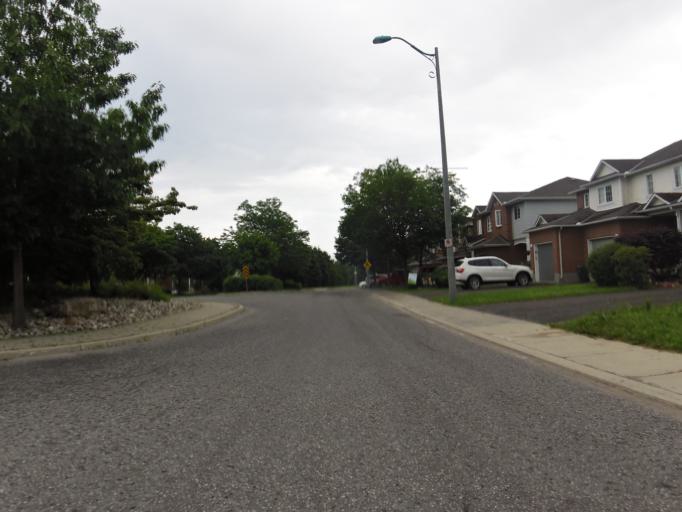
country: CA
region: Ontario
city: Bells Corners
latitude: 45.3189
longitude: -75.8953
